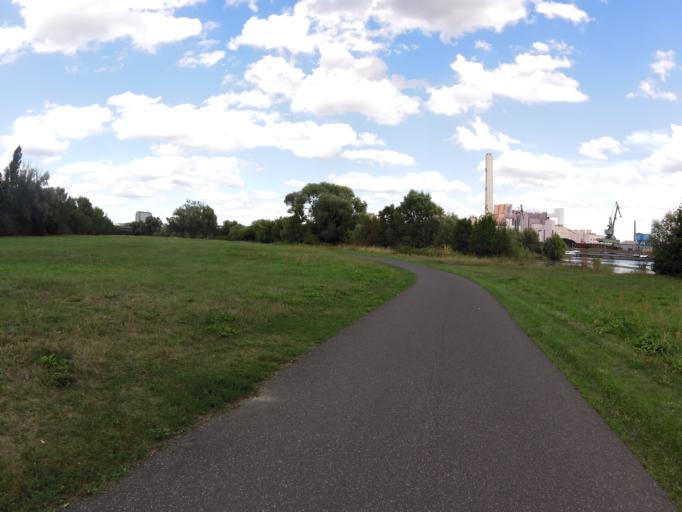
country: DE
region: Bavaria
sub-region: Regierungsbezirk Unterfranken
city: Schweinfurt
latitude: 50.0283
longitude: 10.2172
